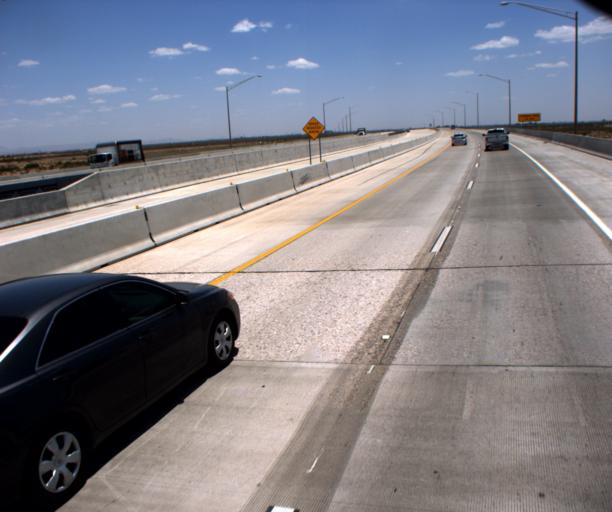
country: US
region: Arizona
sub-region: Maricopa County
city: Queen Creek
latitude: 33.3226
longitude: -111.6442
